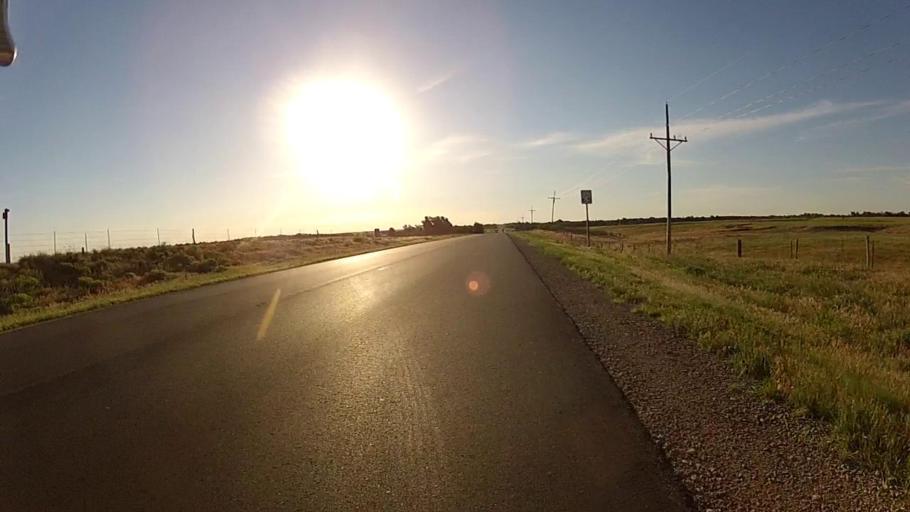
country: US
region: Kansas
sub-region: Comanche County
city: Coldwater
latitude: 37.2809
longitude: -99.2165
